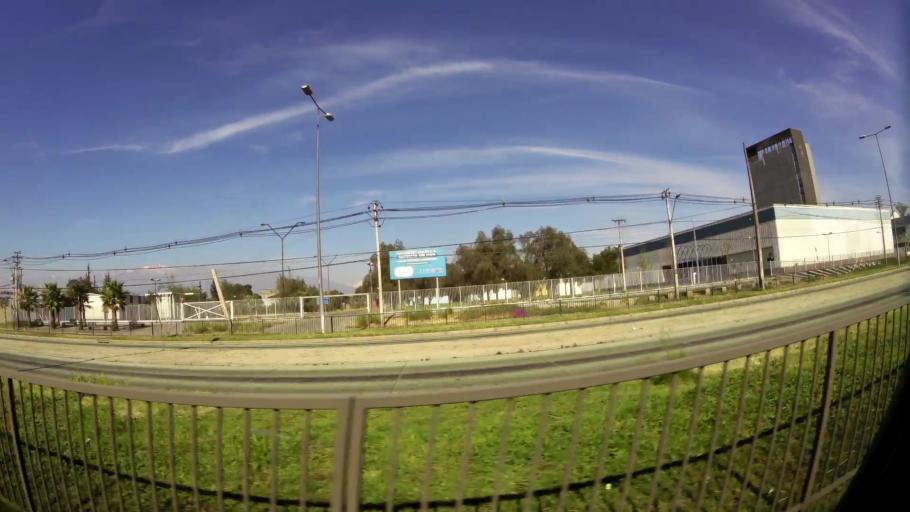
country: CL
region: Santiago Metropolitan
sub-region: Provincia de Santiago
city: Lo Prado
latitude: -33.4879
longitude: -70.7001
